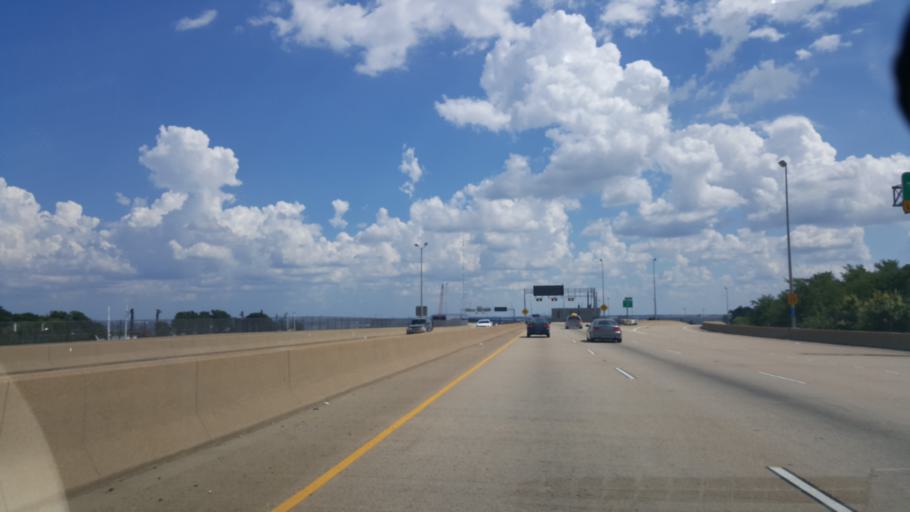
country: US
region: Virginia
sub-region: City of Newport News
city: Newport News
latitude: 36.9700
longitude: -76.4172
